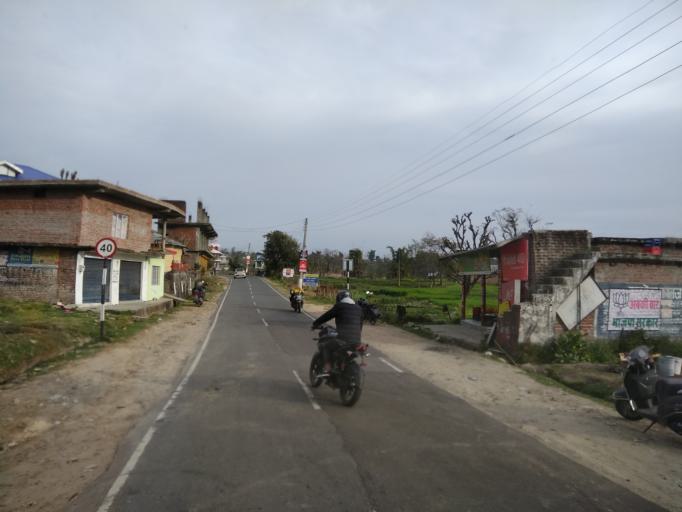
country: IN
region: Himachal Pradesh
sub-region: Kangra
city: Palampur
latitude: 32.1104
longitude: 76.4927
